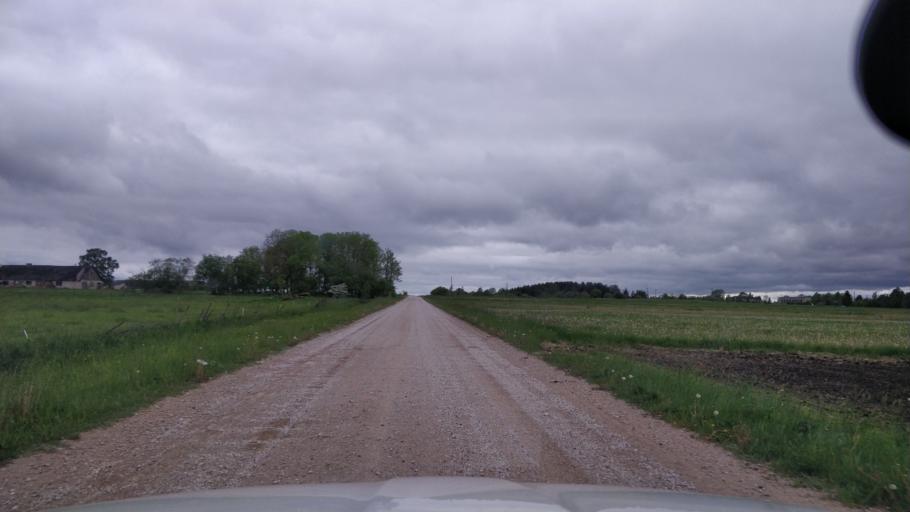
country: EE
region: Raplamaa
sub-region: Maerjamaa vald
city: Marjamaa
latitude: 58.7150
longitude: 24.2542
